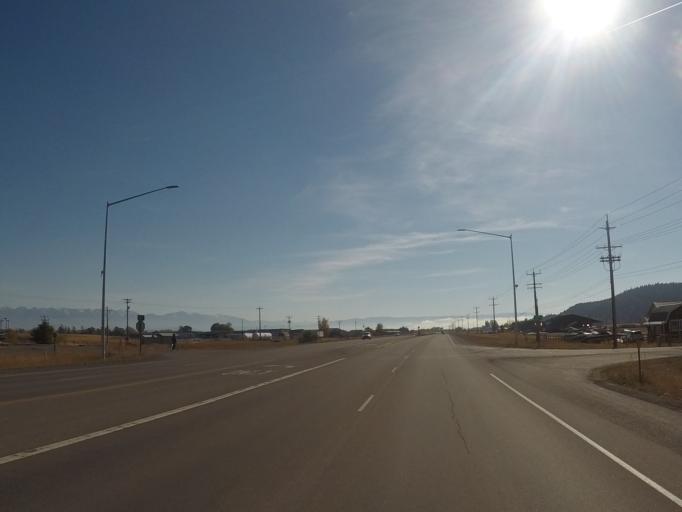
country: US
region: Montana
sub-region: Flathead County
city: Kalispell
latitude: 48.1395
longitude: -114.2788
